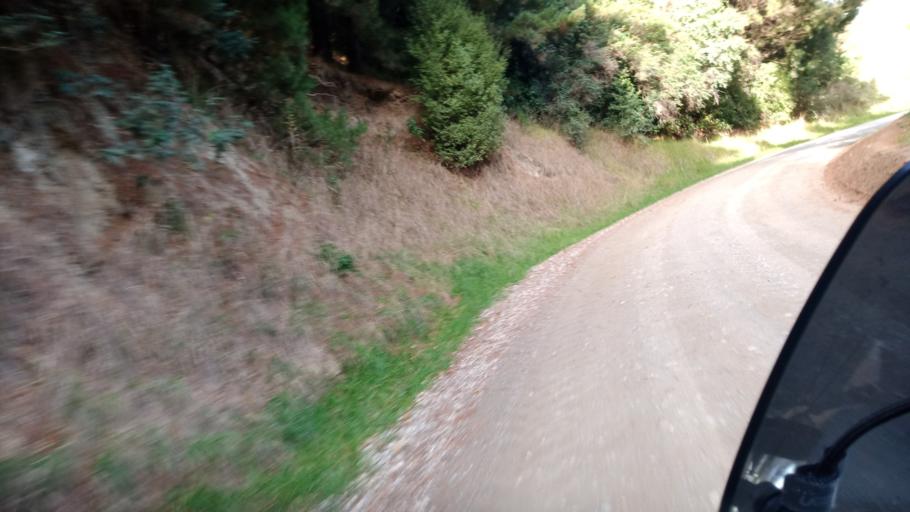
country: NZ
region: Gisborne
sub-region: Gisborne District
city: Gisborne
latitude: -38.5361
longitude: 177.5243
